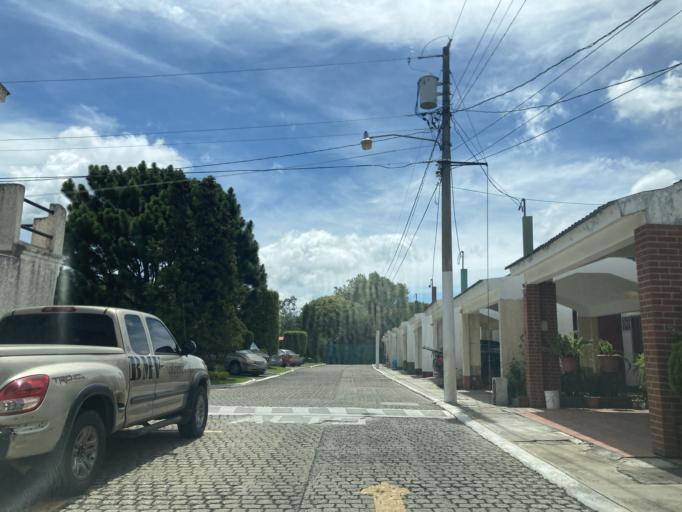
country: GT
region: Guatemala
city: San Jose Pinula
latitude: 14.5425
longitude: -90.4348
